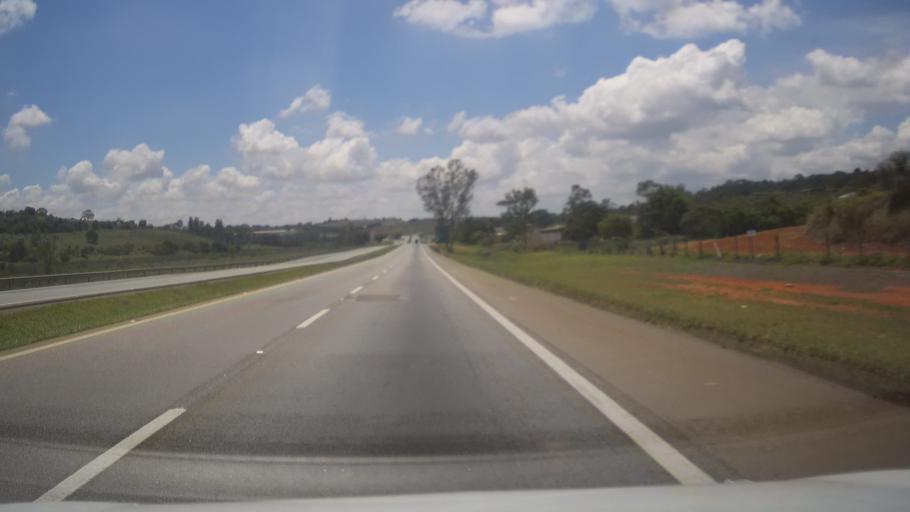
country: BR
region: Minas Gerais
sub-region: Sao Goncalo Do Sapucai
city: Sao Goncalo do Sapucai
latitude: -21.9172
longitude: -45.5895
